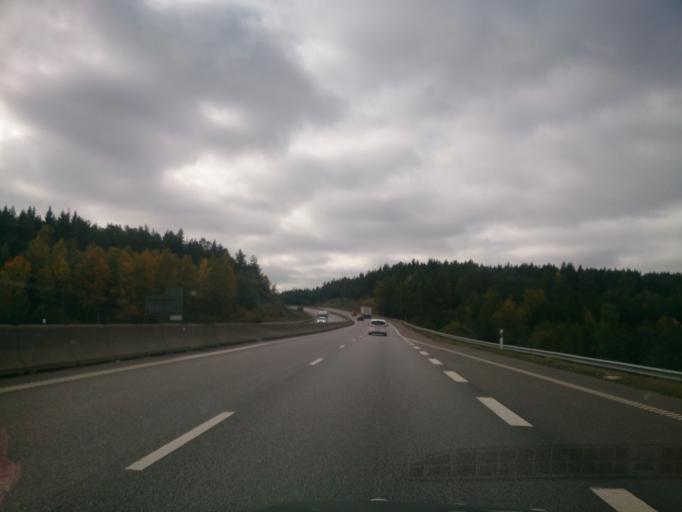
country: SE
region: OEstergoetland
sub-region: Norrkopings Kommun
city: Kimstad
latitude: 58.5477
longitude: 16.0479
